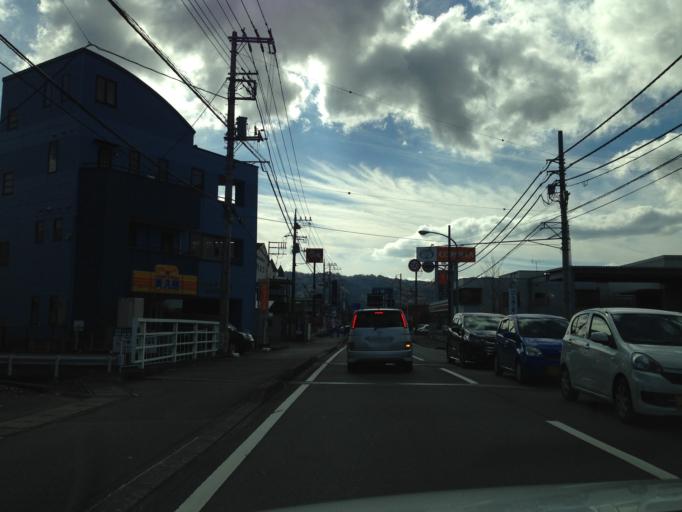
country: JP
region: Shizuoka
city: Mishima
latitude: 35.0078
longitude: 138.9423
